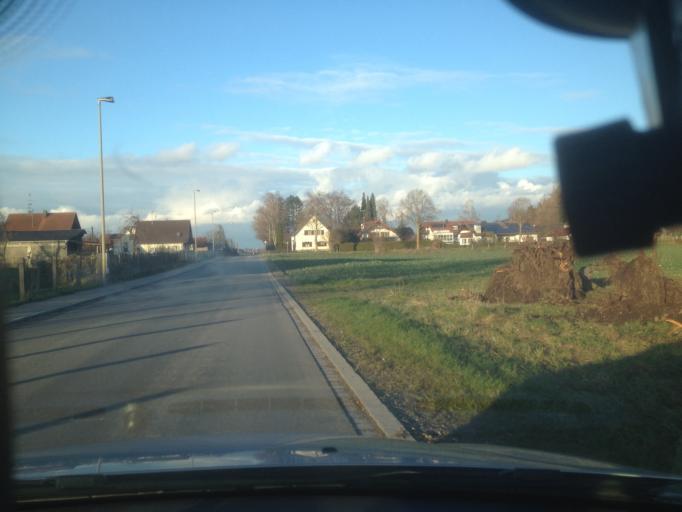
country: DE
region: Bavaria
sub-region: Upper Bavaria
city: Prittriching
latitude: 48.2037
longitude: 10.9318
